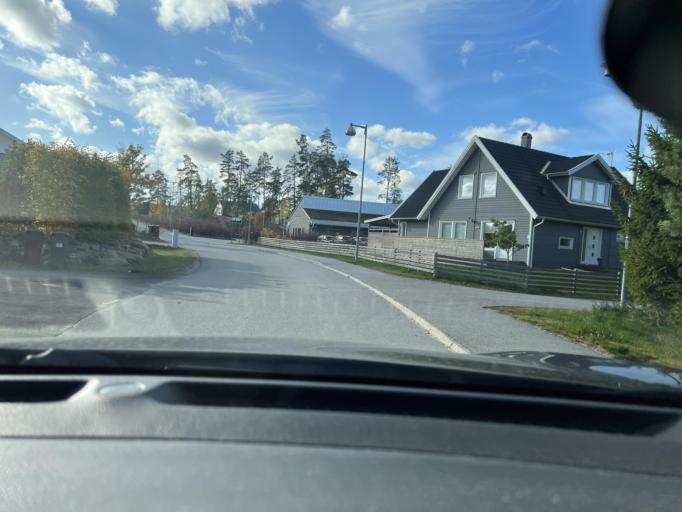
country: SE
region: Stockholm
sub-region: Vallentuna Kommun
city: Vallentuna
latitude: 59.5054
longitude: 18.0810
